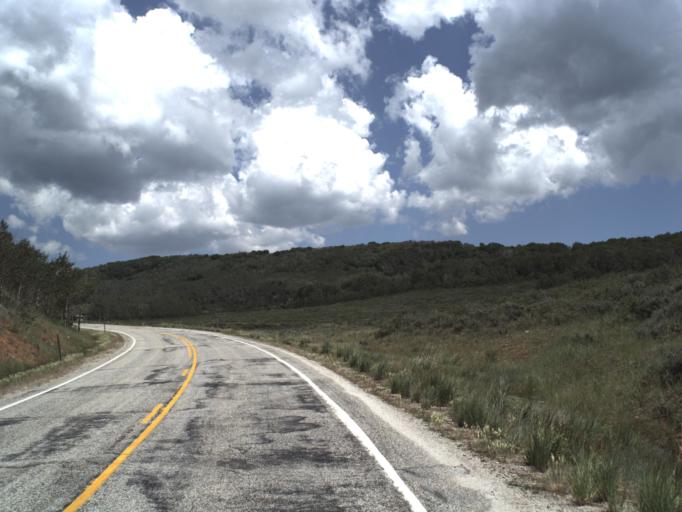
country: US
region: Utah
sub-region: Weber County
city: Wolf Creek
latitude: 41.4079
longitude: -111.5925
